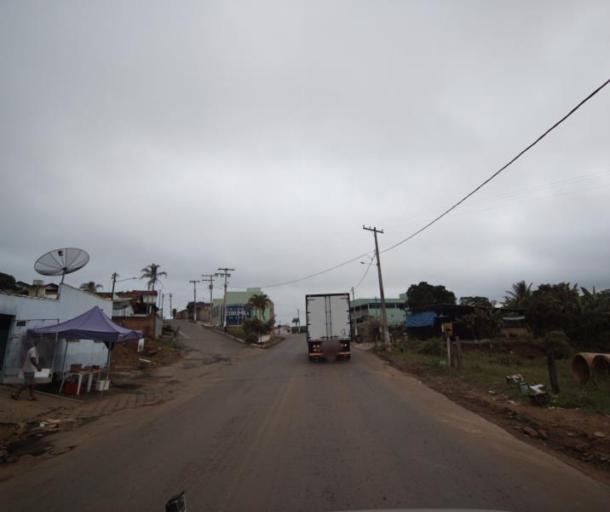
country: BR
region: Goias
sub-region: Pirenopolis
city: Pirenopolis
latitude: -15.9315
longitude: -48.8051
